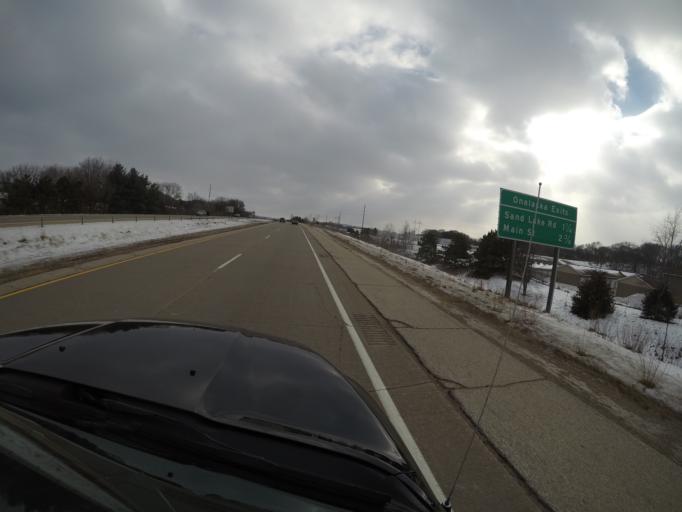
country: US
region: Wisconsin
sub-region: La Crosse County
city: Onalaska
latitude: 43.9156
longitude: -91.2377
